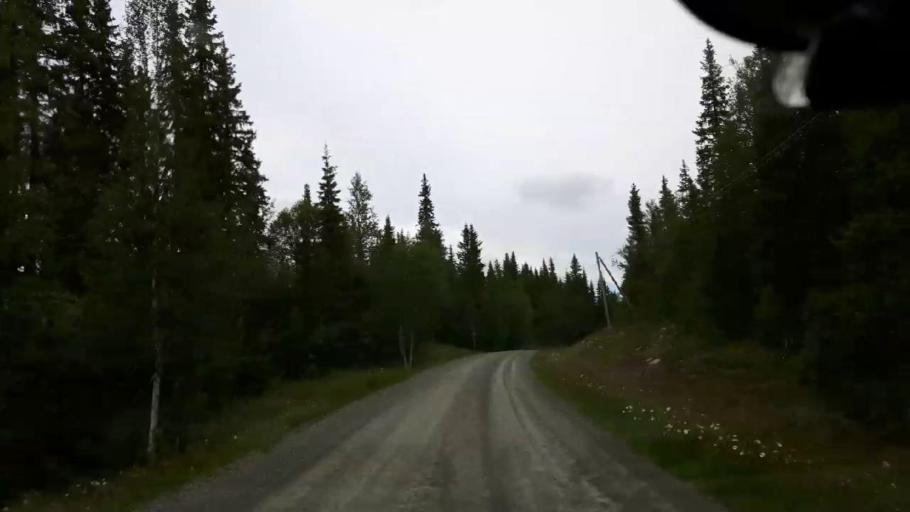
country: SE
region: Jaemtland
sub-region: Krokoms Kommun
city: Valla
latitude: 63.7306
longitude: 13.8360
